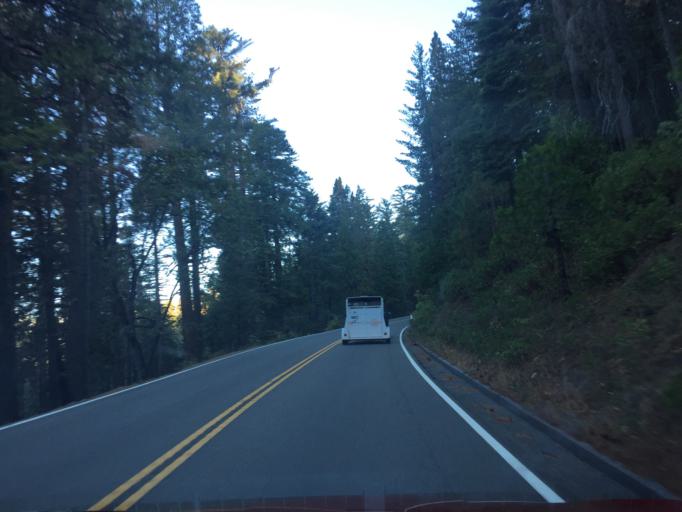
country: US
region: California
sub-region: Mariposa County
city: Yosemite Valley
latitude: 37.6401
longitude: -119.6961
